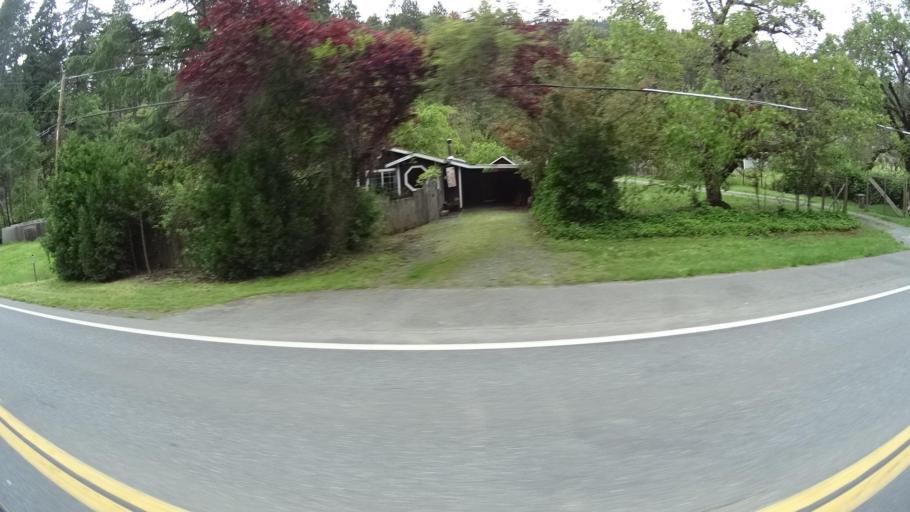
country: US
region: California
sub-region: Humboldt County
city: Willow Creek
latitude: 40.9693
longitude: -123.6402
